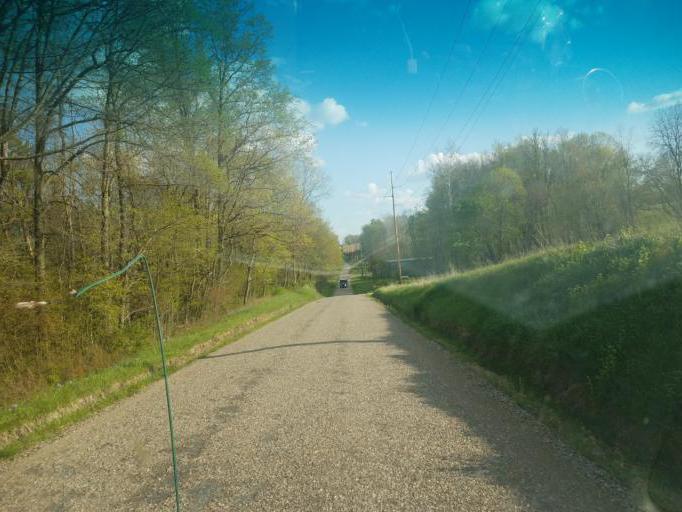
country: US
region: Ohio
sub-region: Wayne County
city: Shreve
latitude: 40.6596
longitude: -82.0335
